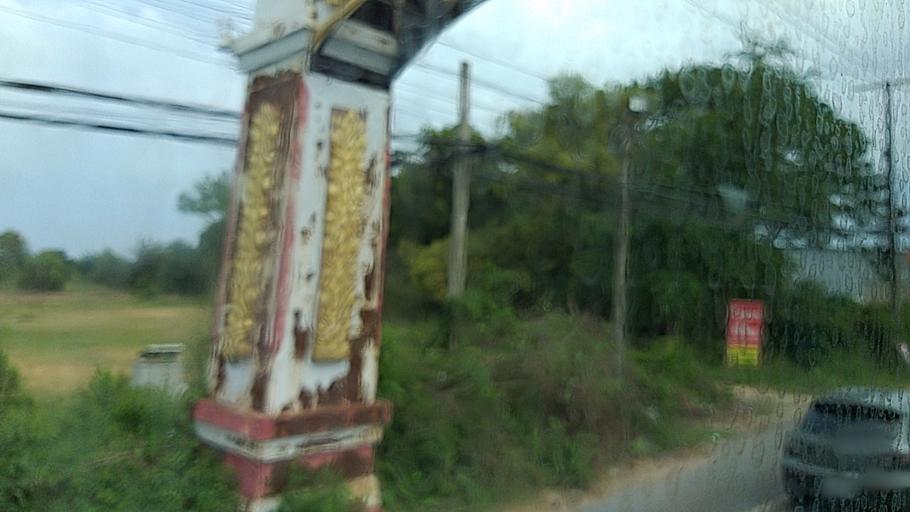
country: TH
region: Roi Et
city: Roi Et
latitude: 16.0630
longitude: 103.6207
